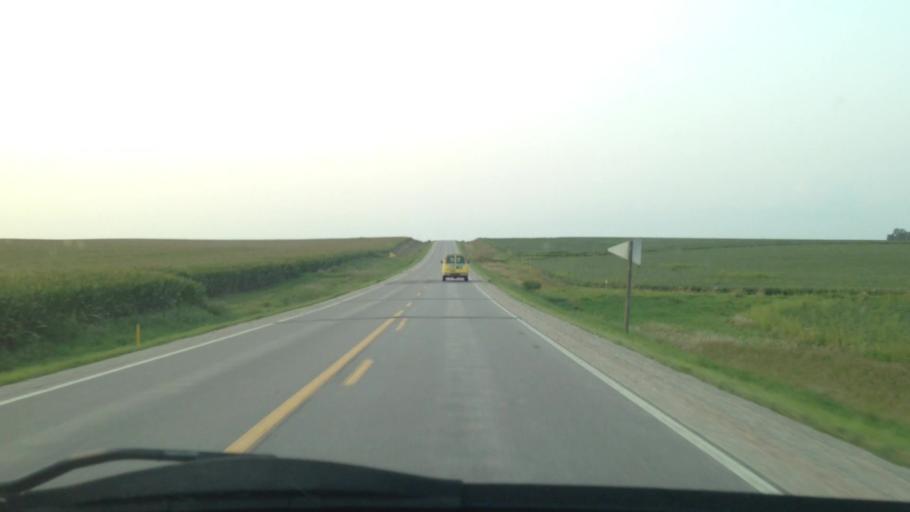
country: US
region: Iowa
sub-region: Benton County
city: Atkins
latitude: 42.0268
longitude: -91.8740
